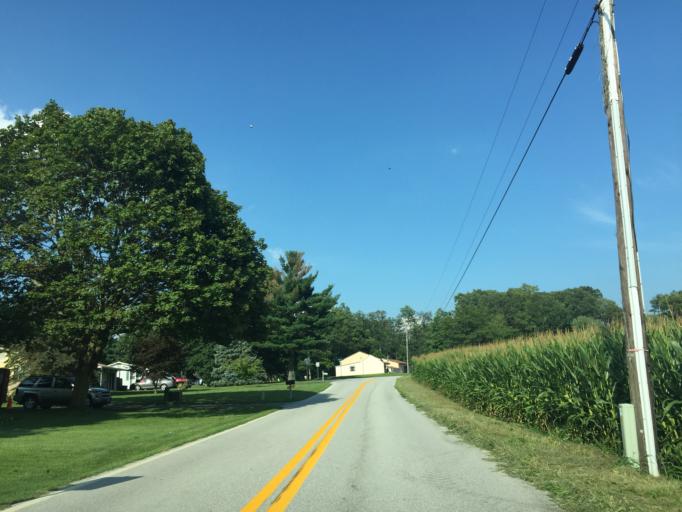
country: US
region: Maryland
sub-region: Carroll County
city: Hampstead
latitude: 39.6470
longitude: -76.8314
